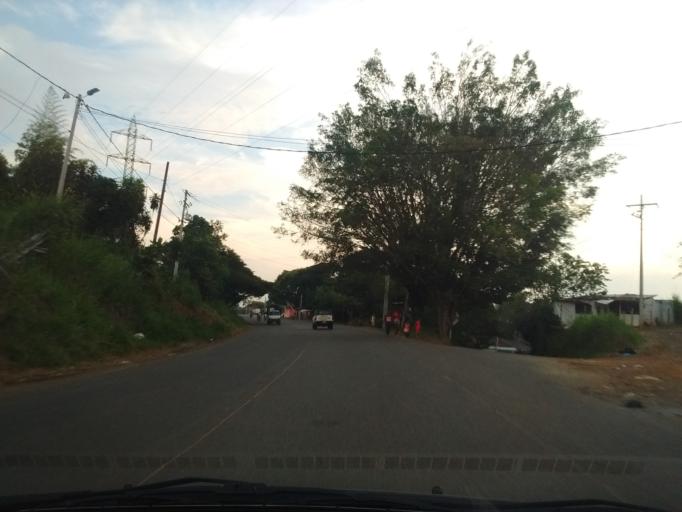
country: CO
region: Cauca
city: Santander de Quilichao
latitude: 2.9992
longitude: -76.4933
